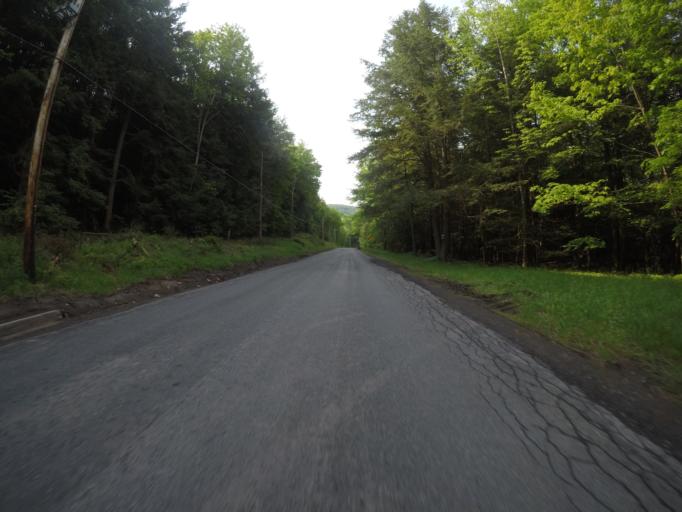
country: US
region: New York
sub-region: Sullivan County
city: Livingston Manor
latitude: 42.0929
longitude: -74.7914
